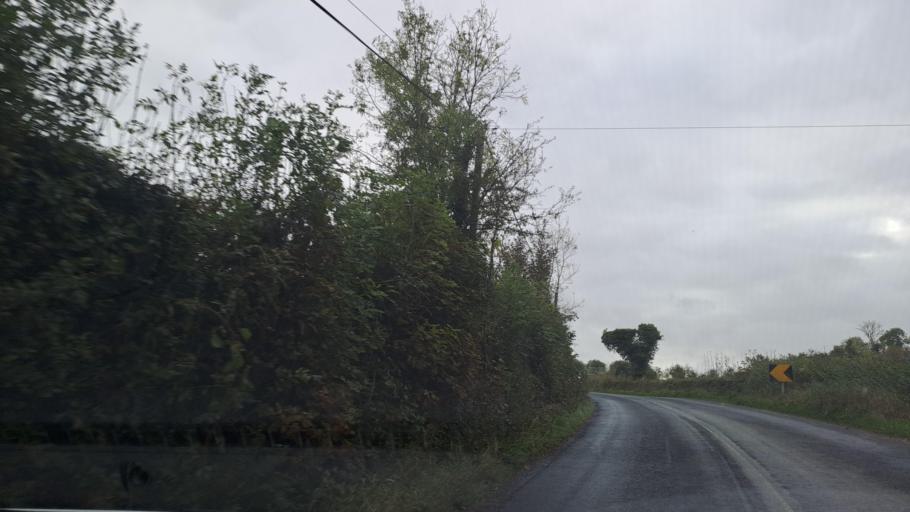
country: IE
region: Ulster
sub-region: An Cabhan
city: Cootehill
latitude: 53.9984
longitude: -7.0549
